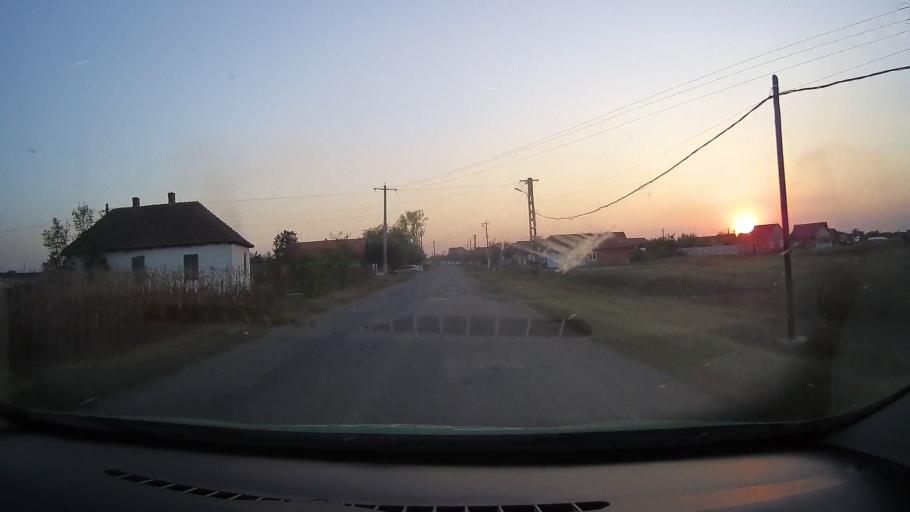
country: RO
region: Arad
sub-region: Comuna Olari
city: Olari
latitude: 46.3903
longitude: 21.5518
